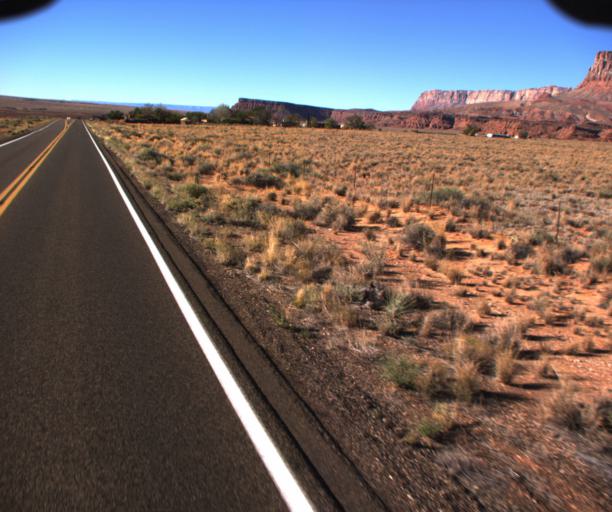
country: US
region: Arizona
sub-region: Coconino County
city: Page
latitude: 36.7931
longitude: -111.6819
